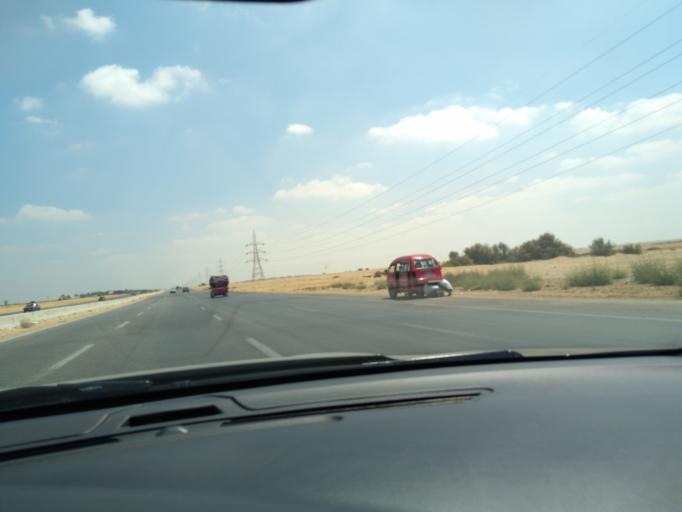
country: EG
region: Al Isma'iliyah
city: At Tall al Kabir
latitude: 30.3756
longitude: 31.9353
